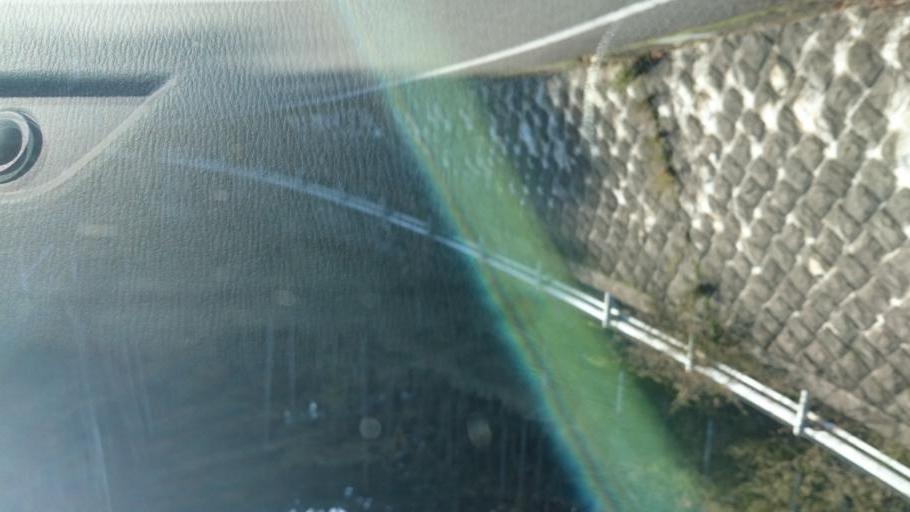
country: JP
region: Shizuoka
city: Heda
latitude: 35.0042
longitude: 138.8319
